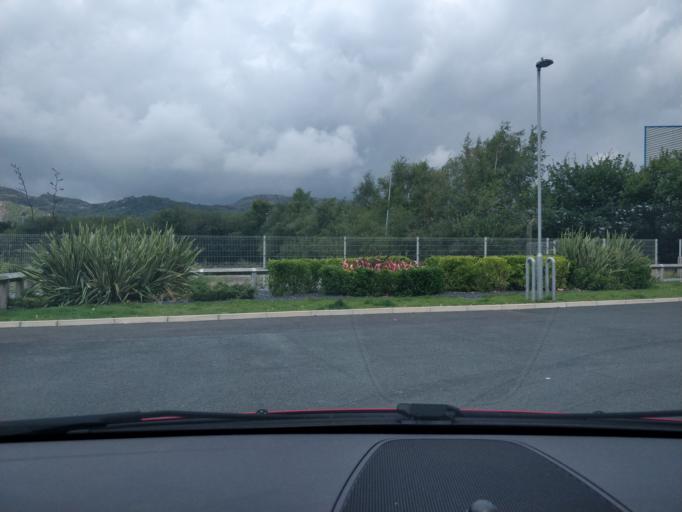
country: GB
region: Wales
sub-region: Gwynedd
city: Porthmadog
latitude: 52.9299
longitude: -4.1380
